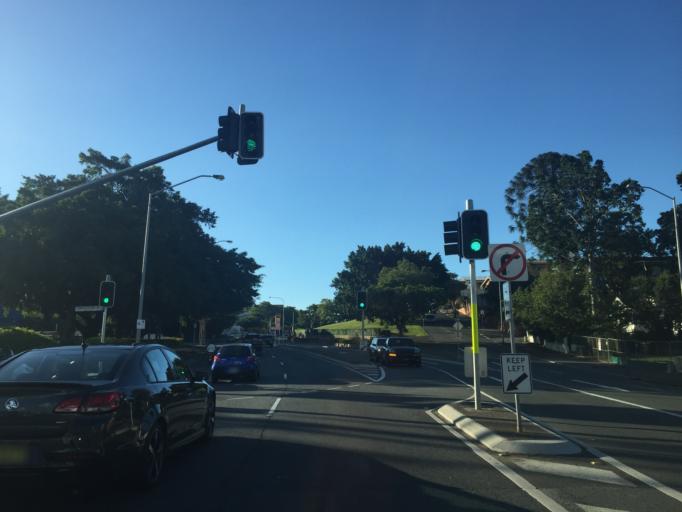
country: AU
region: Queensland
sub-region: Brisbane
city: Windsor
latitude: -27.4327
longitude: 153.0320
